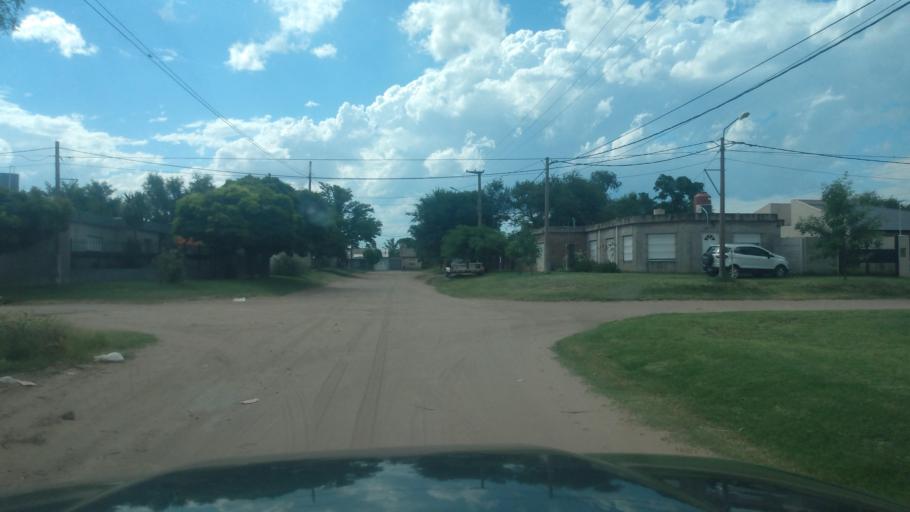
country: AR
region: La Pampa
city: Santa Rosa
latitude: -36.6443
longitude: -64.2847
